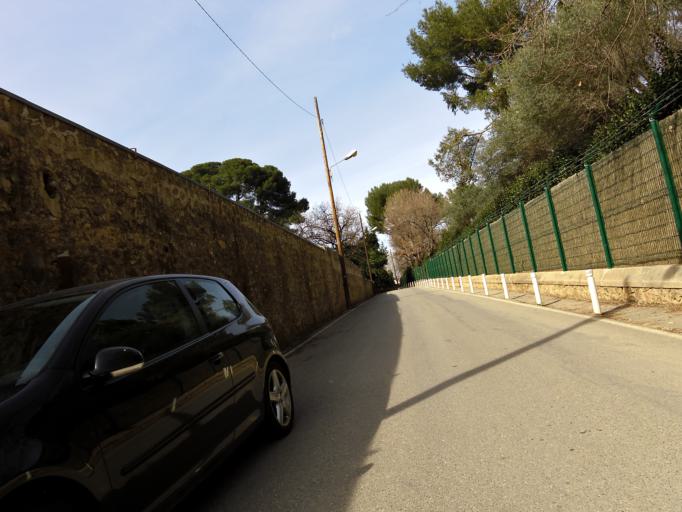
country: FR
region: Provence-Alpes-Cote d'Azur
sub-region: Departement des Alpes-Maritimes
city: Antibes
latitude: 43.5494
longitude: 7.1298
